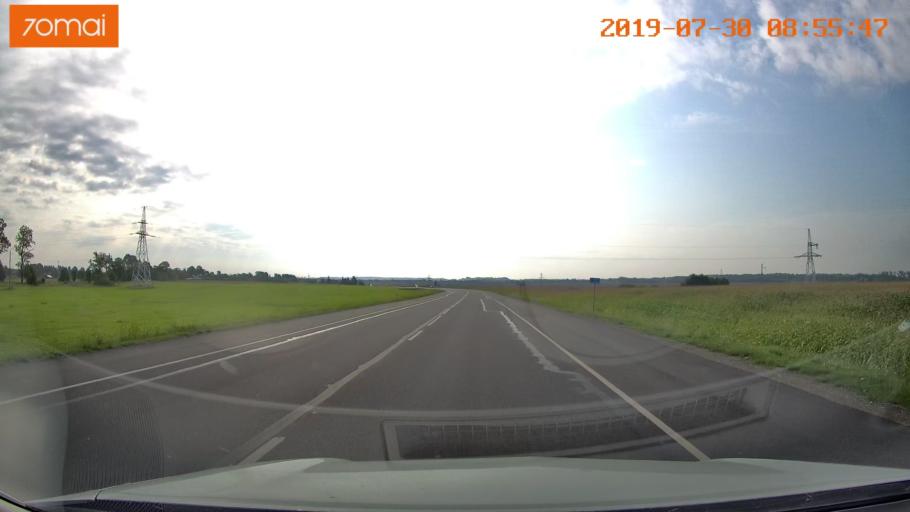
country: RU
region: Kaliningrad
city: Gusev
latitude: 54.5996
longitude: 22.0599
